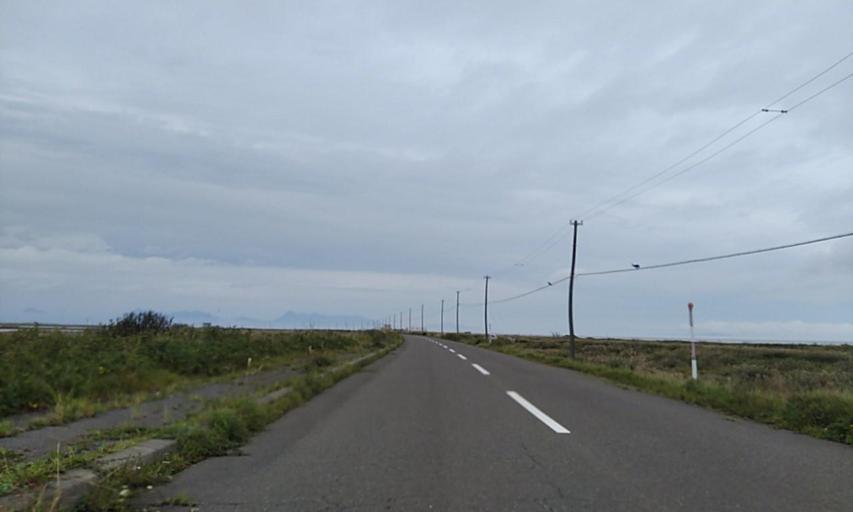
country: JP
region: Hokkaido
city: Shibetsu
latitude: 43.5766
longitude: 145.3447
